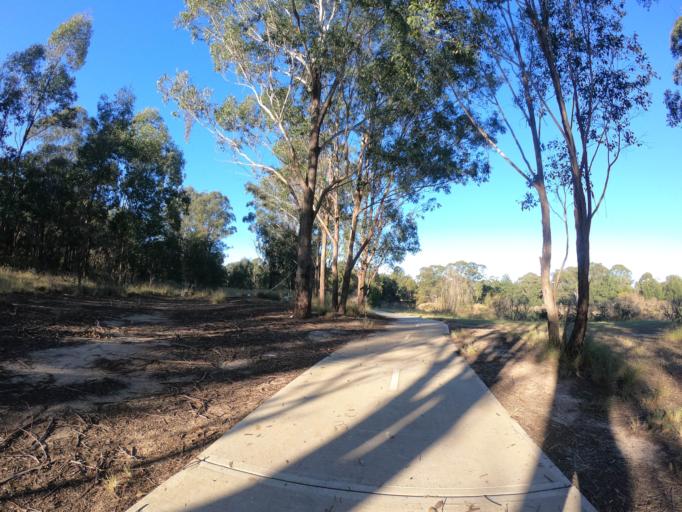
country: AU
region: New South Wales
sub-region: Hawkesbury
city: South Windsor
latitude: -33.6339
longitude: 150.8113
